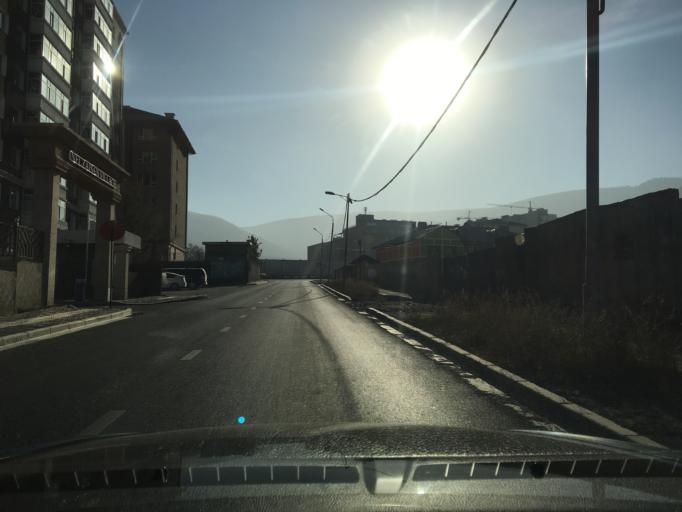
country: MN
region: Ulaanbaatar
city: Ulaanbaatar
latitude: 47.8783
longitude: 106.9120
